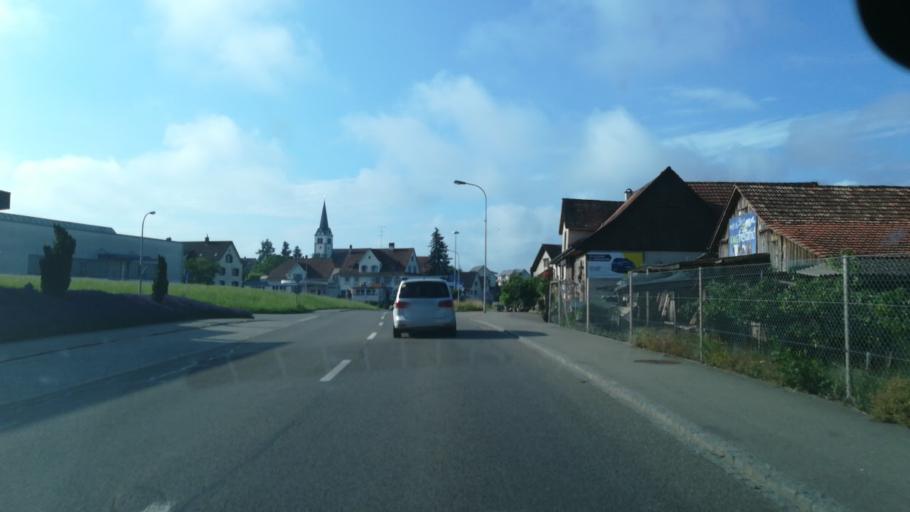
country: CH
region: Thurgau
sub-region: Weinfelden District
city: Sulgen
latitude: 47.5462
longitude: 9.1808
